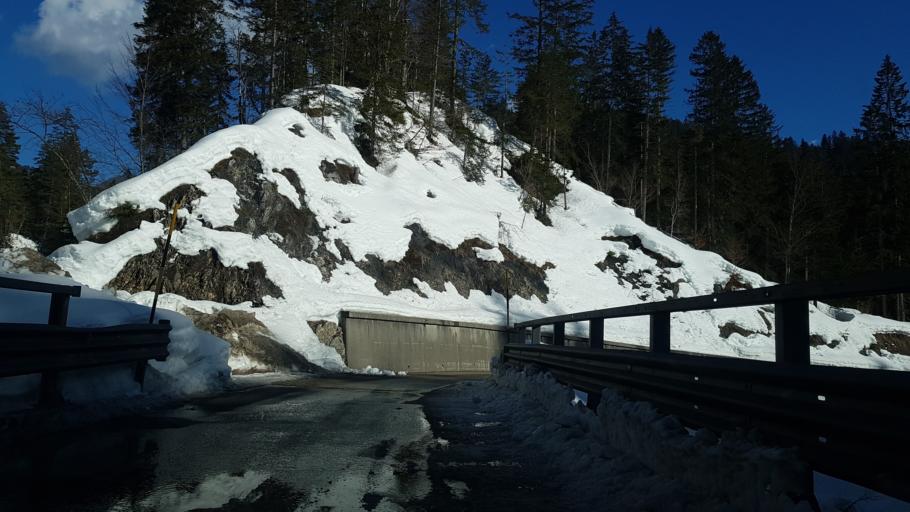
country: IT
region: Friuli Venezia Giulia
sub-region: Provincia di Udine
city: Malborghetto
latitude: 46.5286
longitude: 13.4738
